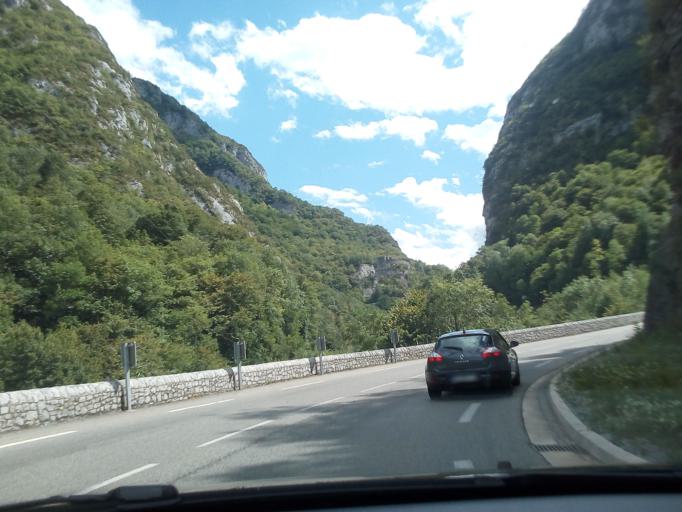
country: FR
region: Aquitaine
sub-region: Departement des Pyrenees-Atlantiques
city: Laruns
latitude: 42.8928
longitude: -0.5642
